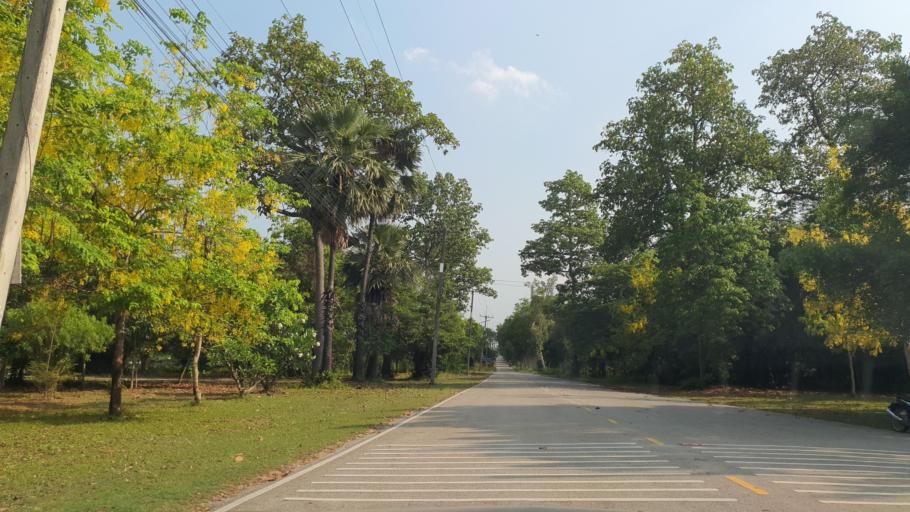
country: TH
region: Chiang Mai
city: San Pa Tong
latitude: 18.6499
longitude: 98.8482
